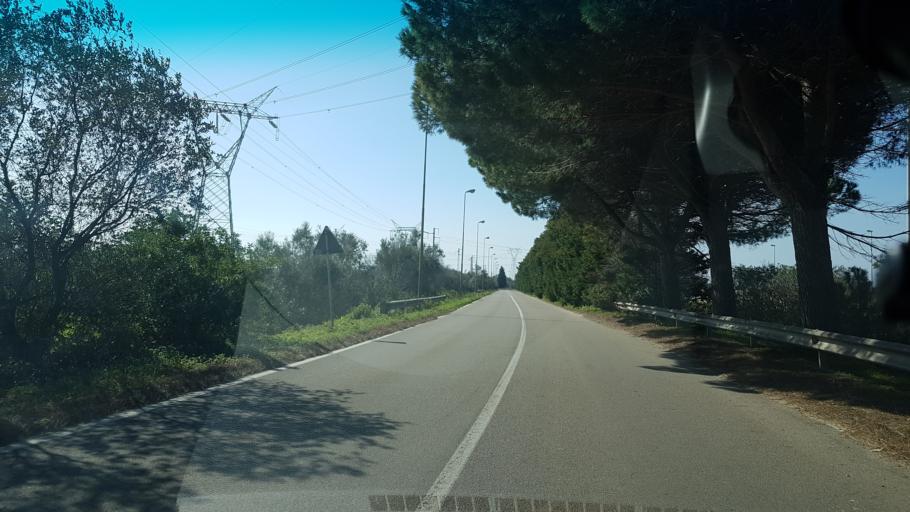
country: IT
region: Apulia
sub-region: Provincia di Brindisi
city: Torchiarolo
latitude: 40.5578
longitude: 18.0333
